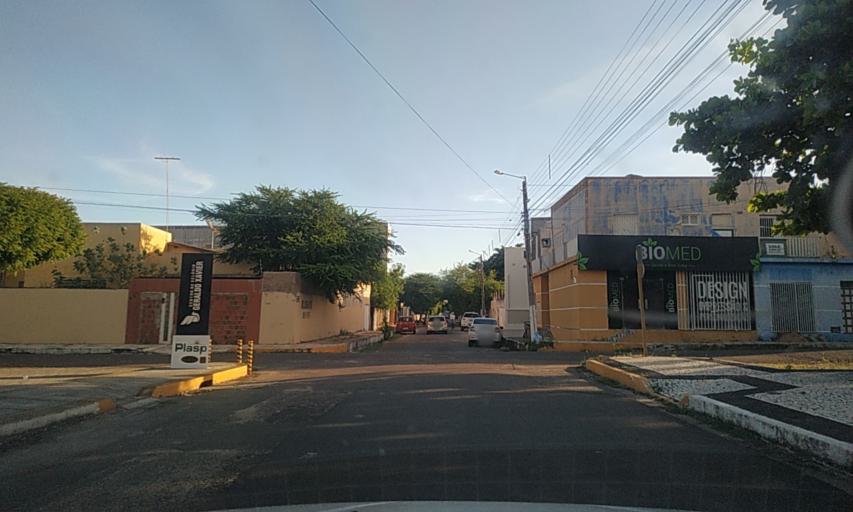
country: BR
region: Rio Grande do Norte
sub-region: Mossoro
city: Mossoro
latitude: -5.1909
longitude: -37.3378
